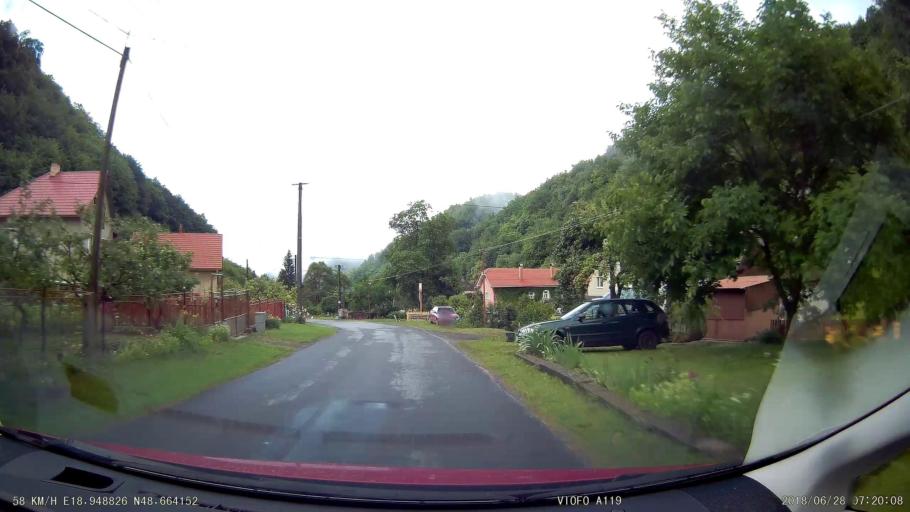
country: SK
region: Banskobystricky
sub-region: Okres Ziar nad Hronom
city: Kremnica
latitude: 48.6640
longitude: 18.9488
